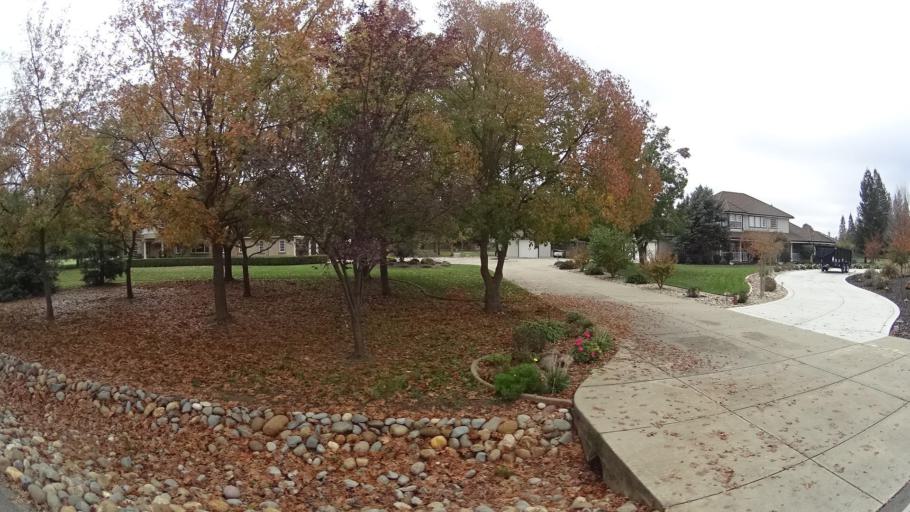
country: US
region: California
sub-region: Sacramento County
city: Wilton
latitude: 38.4499
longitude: -121.3010
